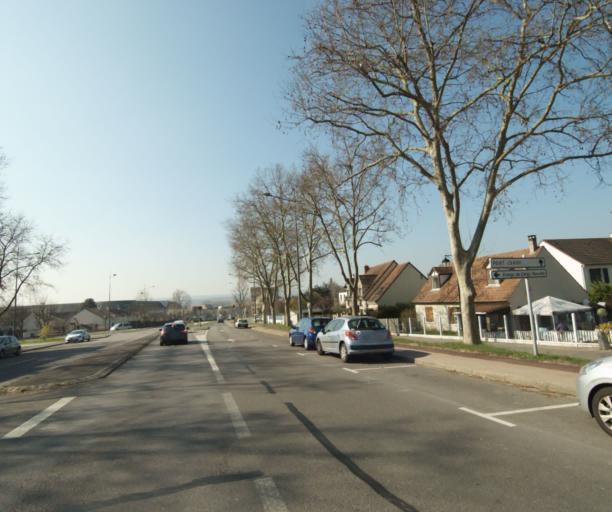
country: FR
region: Ile-de-France
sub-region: Departement du Val-d'Oise
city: Cergy
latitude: 49.0343
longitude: 2.0676
